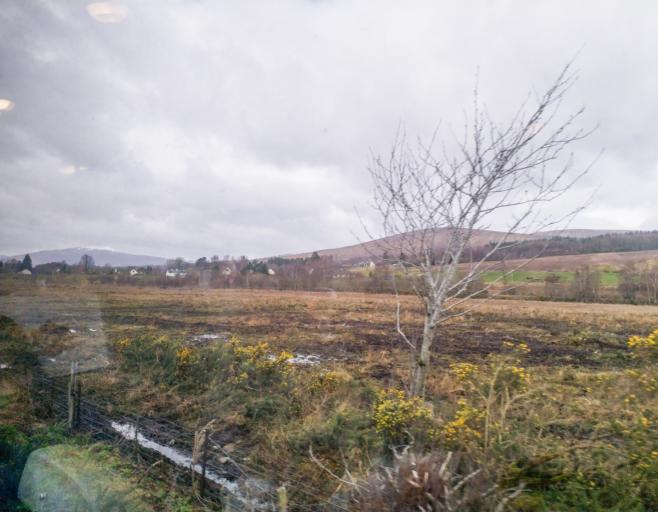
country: GB
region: Scotland
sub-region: Highland
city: Spean Bridge
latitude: 56.8883
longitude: -4.8501
